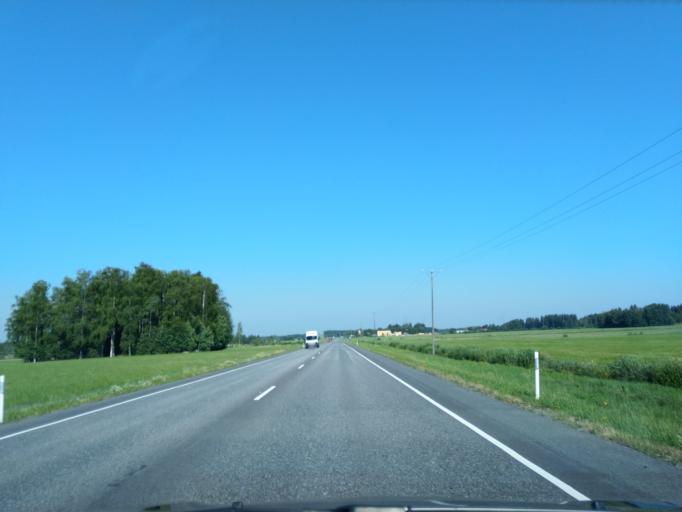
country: FI
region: Pirkanmaa
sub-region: Lounais-Pirkanmaa
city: Punkalaidun
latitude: 61.0341
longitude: 23.0137
